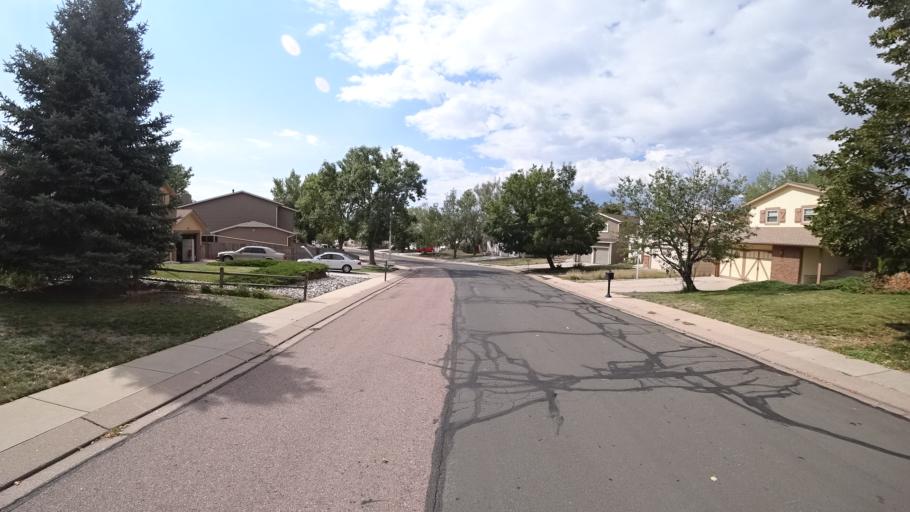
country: US
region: Colorado
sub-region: El Paso County
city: Cimarron Hills
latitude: 38.8524
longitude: -104.7354
